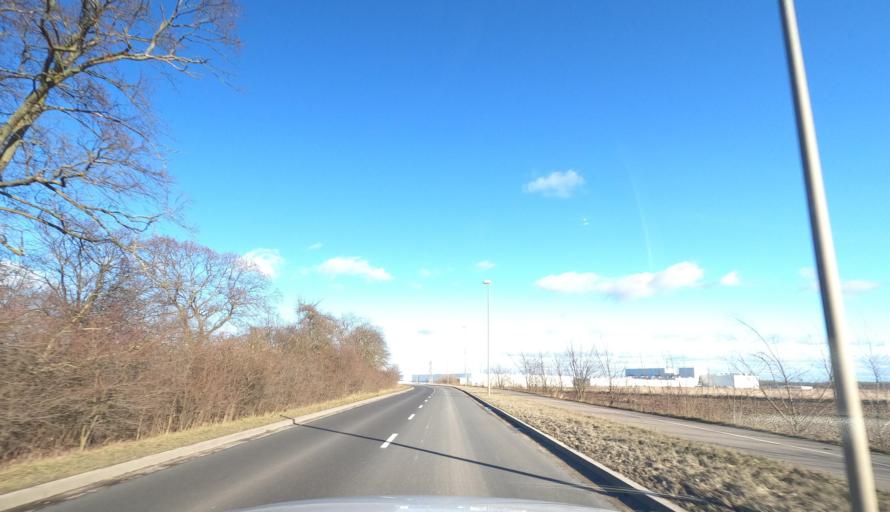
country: PL
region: West Pomeranian Voivodeship
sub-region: Powiat pyrzycki
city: Warnice
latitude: 53.2999
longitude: 14.9670
